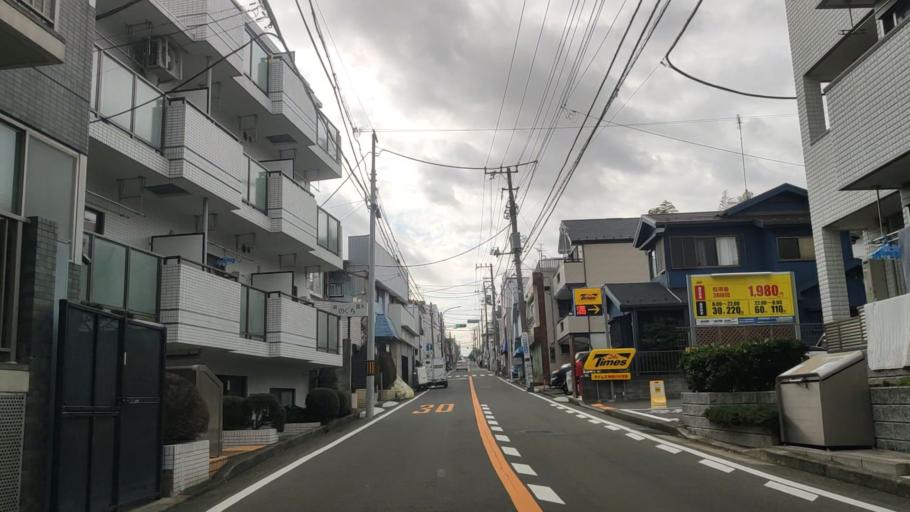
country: JP
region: Kanagawa
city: Yokohama
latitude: 35.4840
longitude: 139.6228
